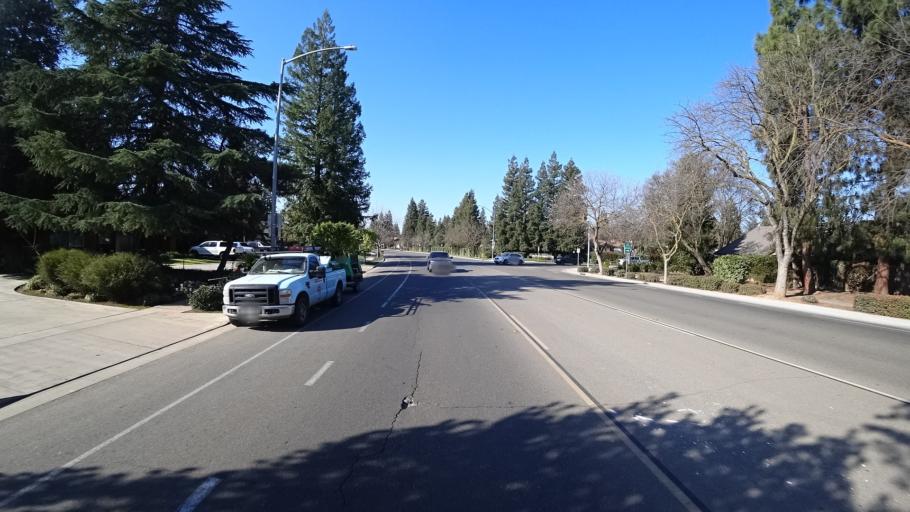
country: US
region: California
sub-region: Fresno County
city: Clovis
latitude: 36.8604
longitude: -119.7948
